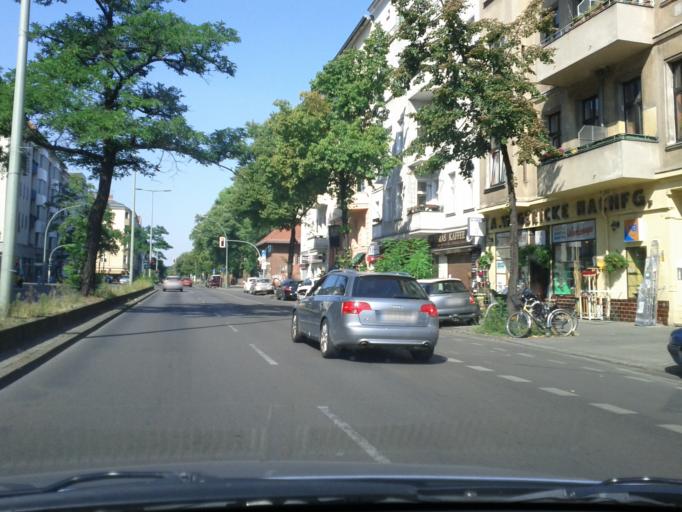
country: DE
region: Berlin
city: Hansaviertel
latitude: 52.5243
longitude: 13.3520
